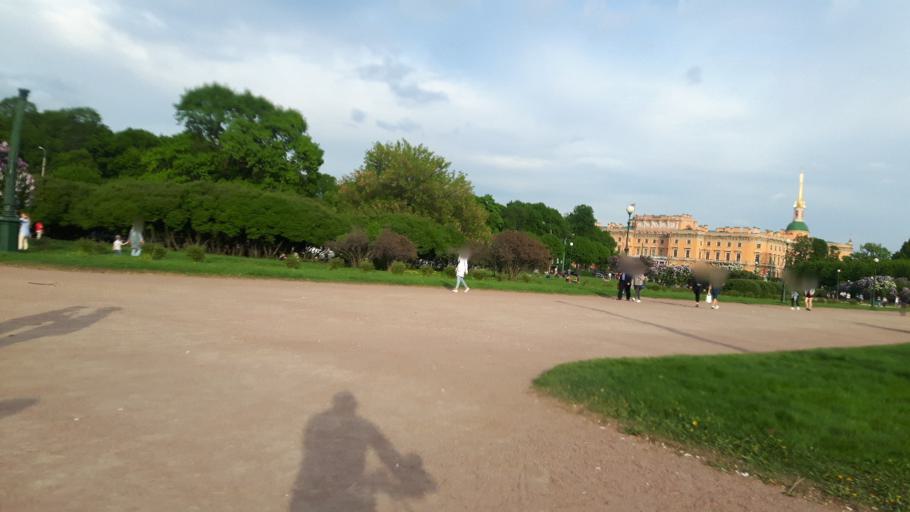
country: RU
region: St.-Petersburg
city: Saint Petersburg
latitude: 59.9429
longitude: 30.3321
